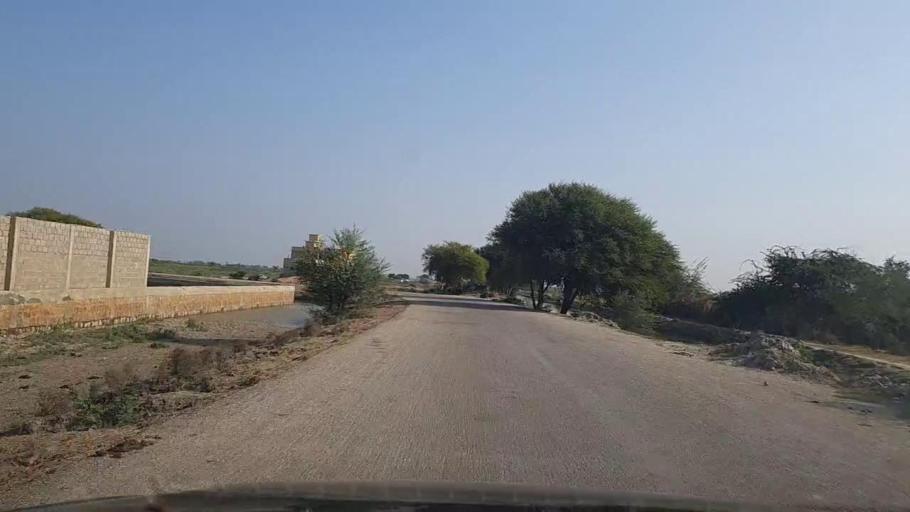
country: PK
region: Sindh
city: Chuhar Jamali
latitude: 24.5888
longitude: 68.0813
